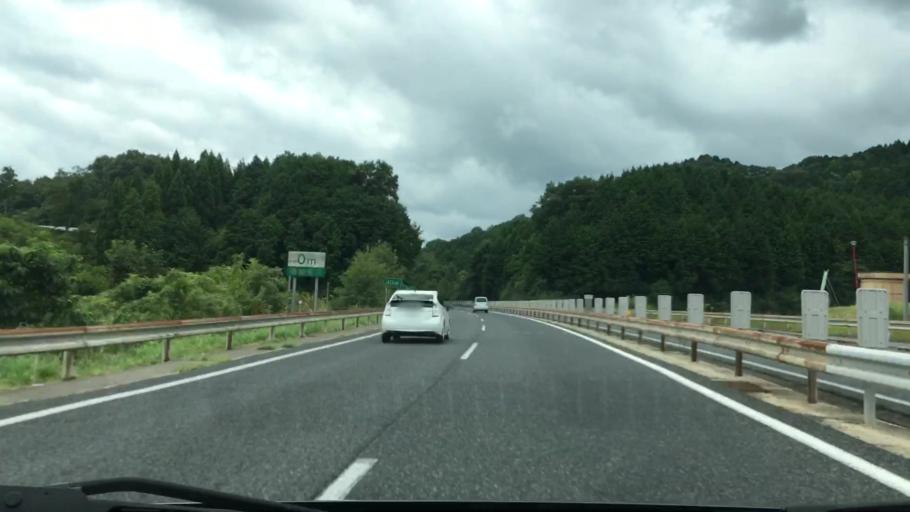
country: JP
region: Okayama
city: Takahashi
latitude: 35.0158
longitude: 133.7301
